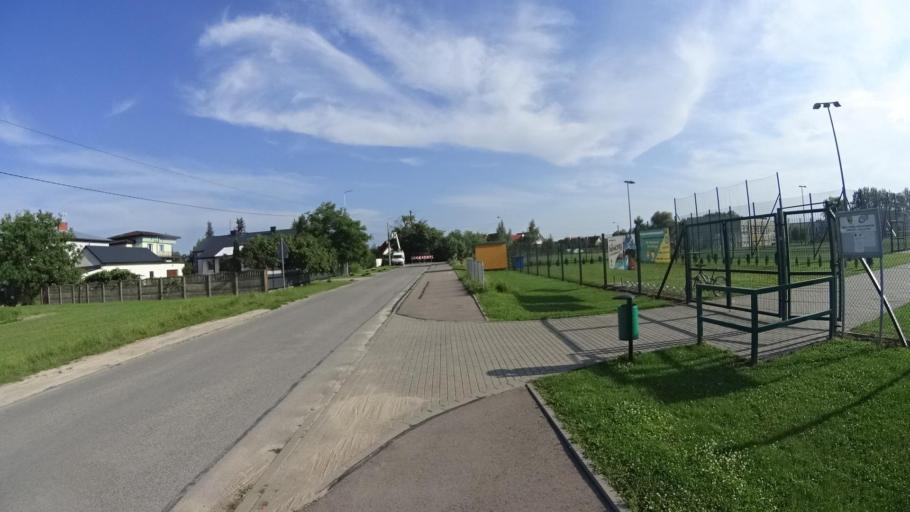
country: PL
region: Masovian Voivodeship
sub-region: Powiat pruszkowski
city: Nadarzyn
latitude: 52.0645
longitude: 20.7887
